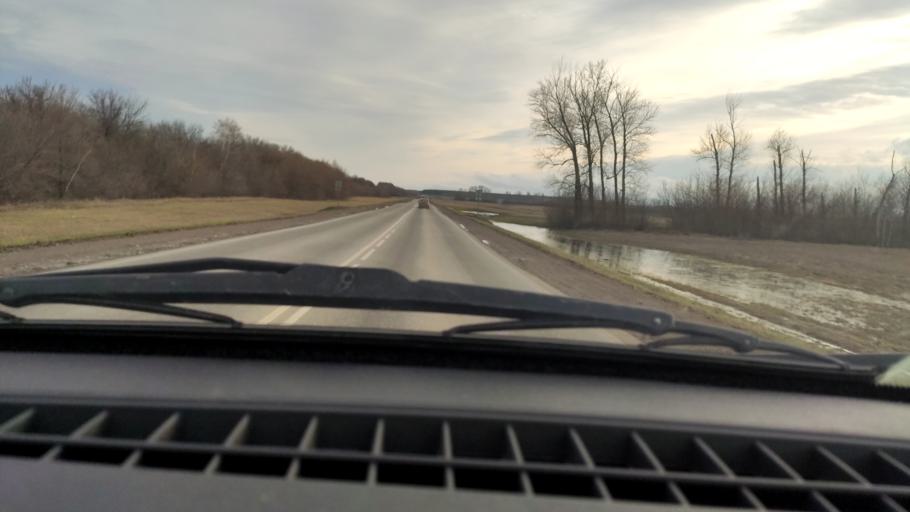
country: RU
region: Bashkortostan
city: Davlekanovo
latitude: 54.2685
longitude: 55.0971
